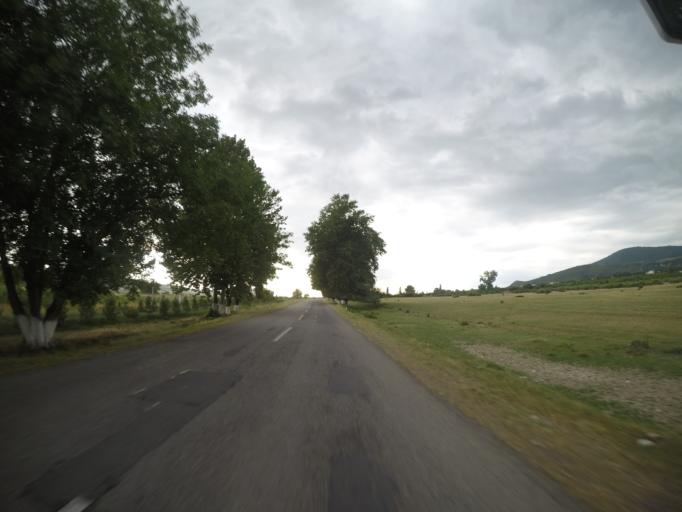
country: AZ
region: Ismayilli
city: Ismayilli
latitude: 40.7535
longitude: 48.2319
